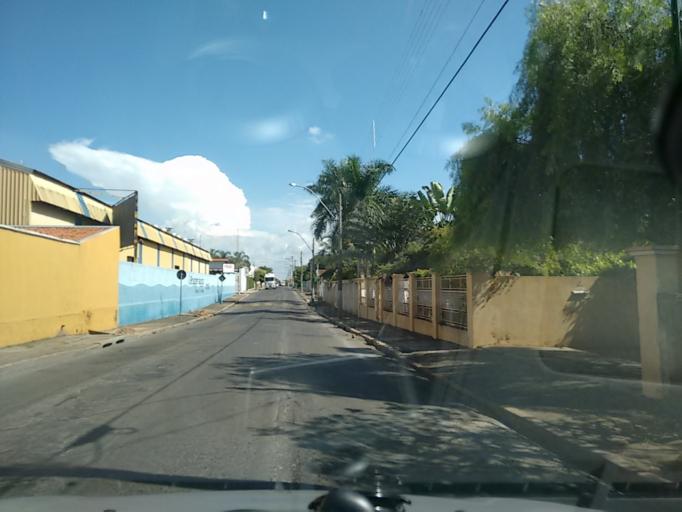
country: BR
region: Sao Paulo
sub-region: Pompeia
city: Pompeia
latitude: -22.1063
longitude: -50.1791
